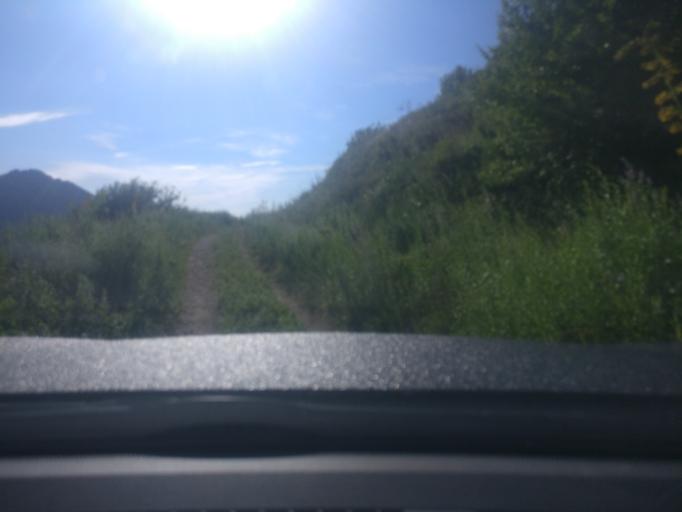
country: KZ
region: Almaty Qalasy
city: Almaty
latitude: 43.1149
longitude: 76.9295
